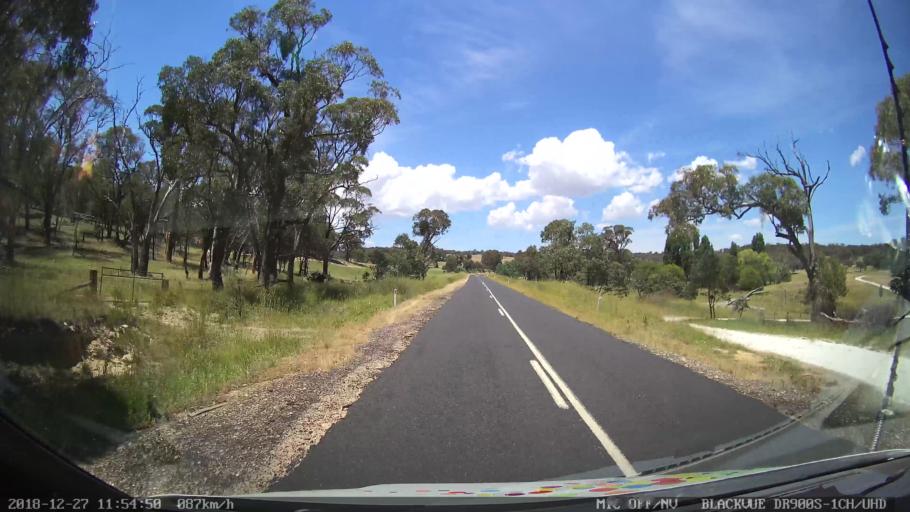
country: AU
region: New South Wales
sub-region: Blayney
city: Blayney
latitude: -33.6800
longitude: 149.4014
